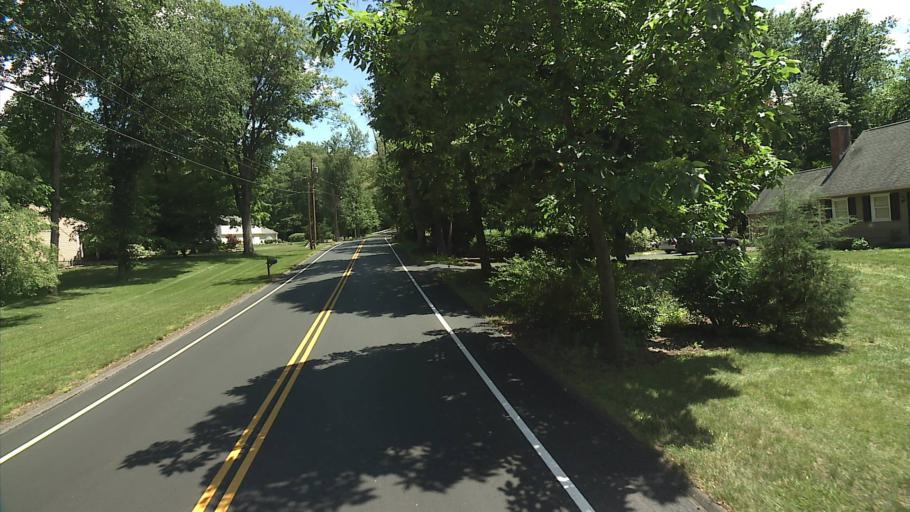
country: US
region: Connecticut
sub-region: Tolland County
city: Somers
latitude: 41.9928
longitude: -72.4276
